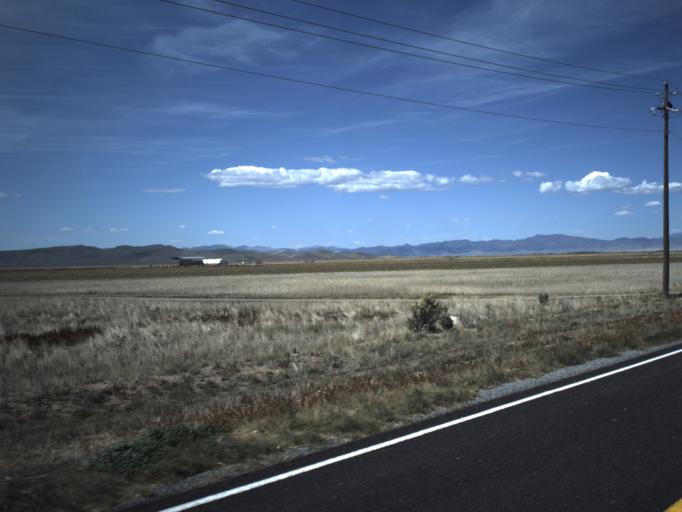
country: US
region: Utah
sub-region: Washington County
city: Enterprise
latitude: 37.6553
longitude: -113.6612
